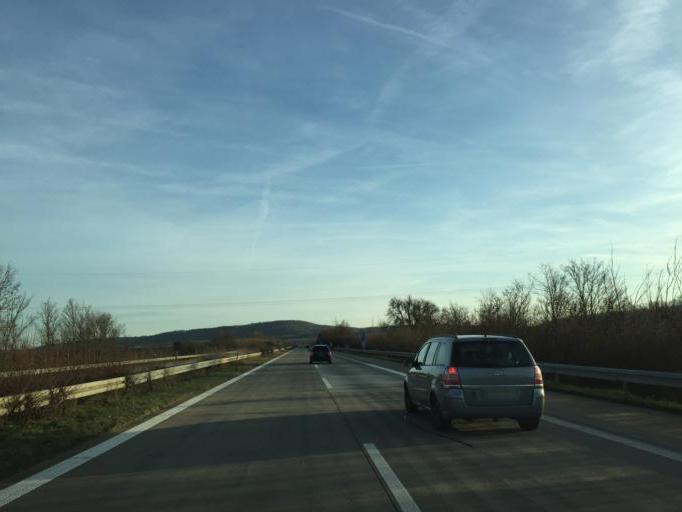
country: DE
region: Bavaria
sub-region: Regierungsbezirk Mittelfranken
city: Gallmersgarten
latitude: 49.4536
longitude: 10.2444
